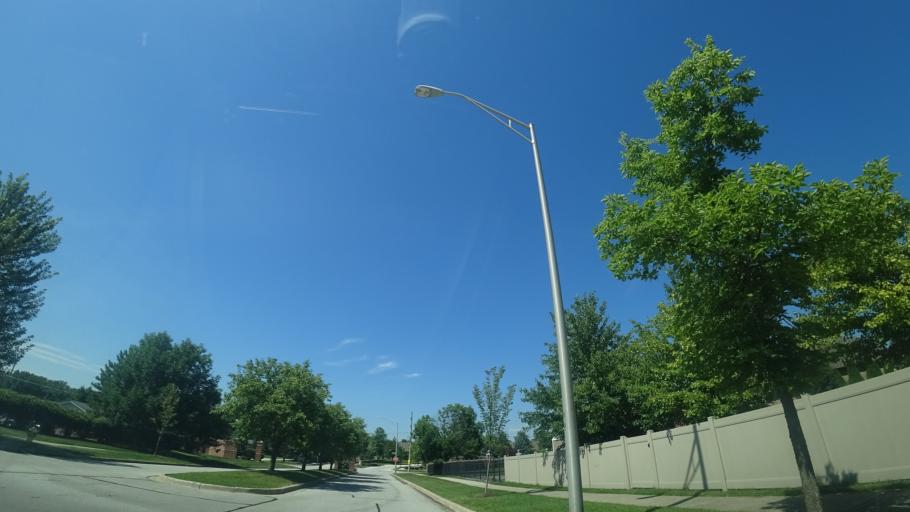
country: US
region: Illinois
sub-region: Will County
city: Mokena
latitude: 41.5635
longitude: -87.8968
